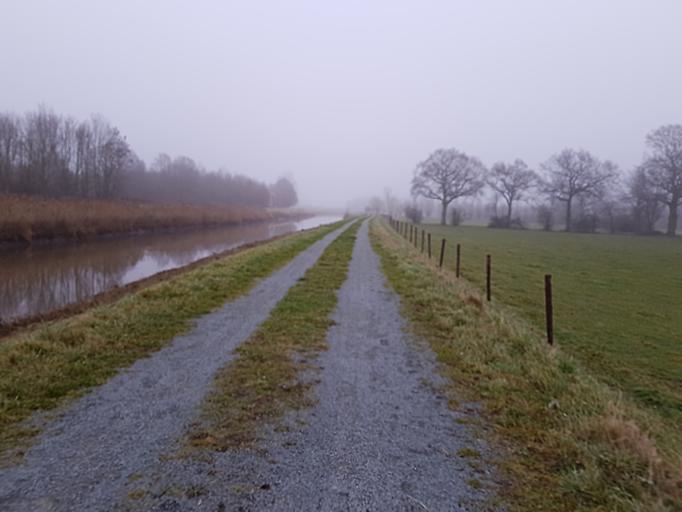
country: BE
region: Flanders
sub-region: Provincie Antwerpen
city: Bonheiden
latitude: 51.0027
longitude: 4.5533
